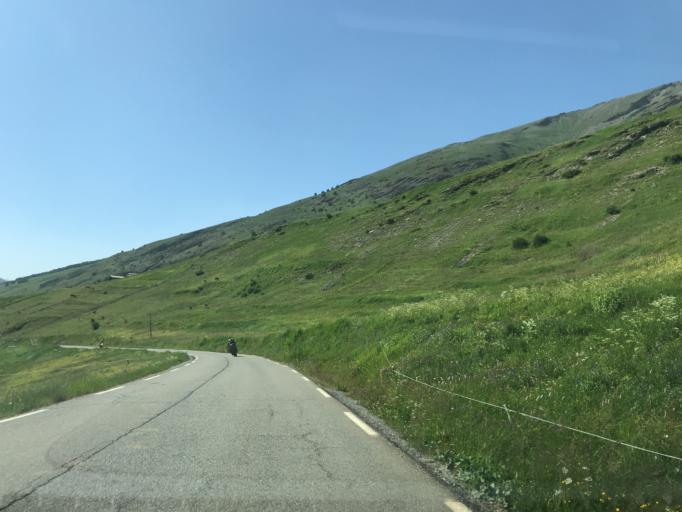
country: IT
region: Piedmont
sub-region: Provincia di Cuneo
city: Pontechianale
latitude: 44.7239
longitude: 6.8822
